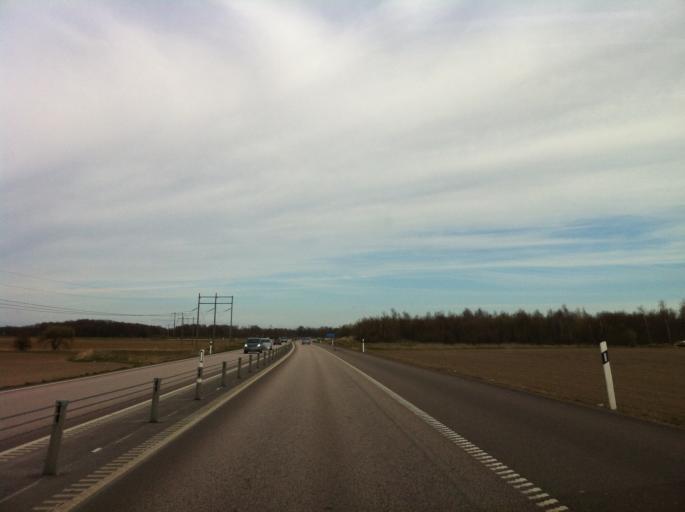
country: SE
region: Skane
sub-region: Helsingborg
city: Odakra
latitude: 56.0934
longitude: 12.6916
